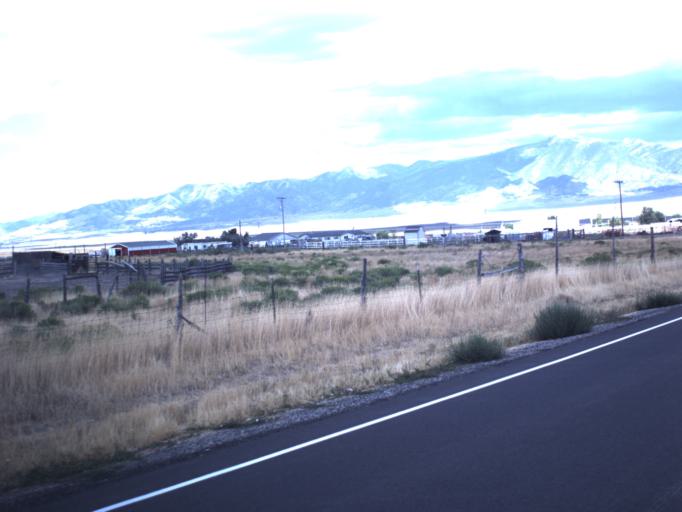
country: US
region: Utah
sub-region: Tooele County
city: Tooele
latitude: 40.3366
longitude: -112.4527
